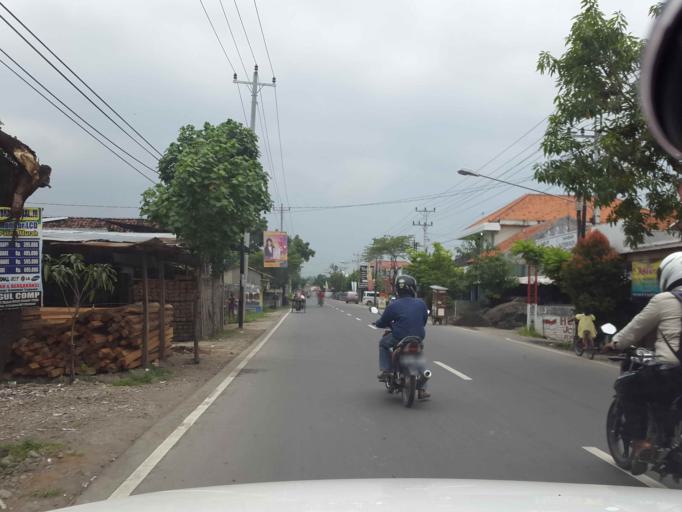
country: ID
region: Central Java
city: Tegal
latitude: -6.8859
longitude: 109.1267
